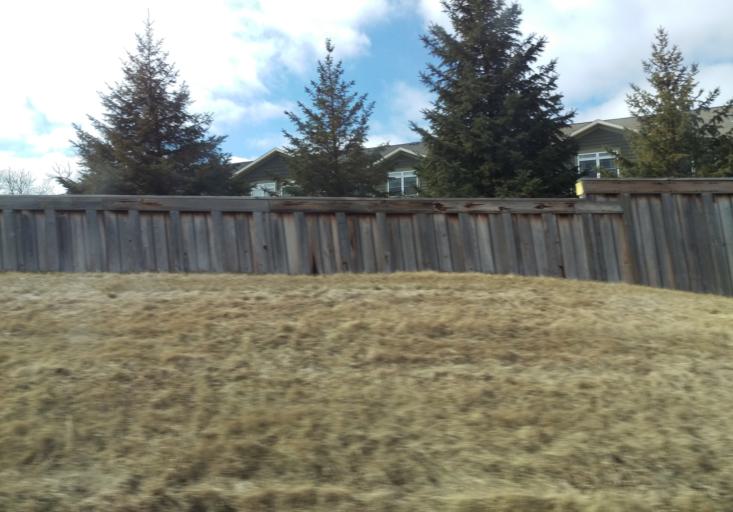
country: US
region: Minnesota
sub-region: Hennepin County
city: Minneapolis
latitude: 44.9420
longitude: -93.2345
